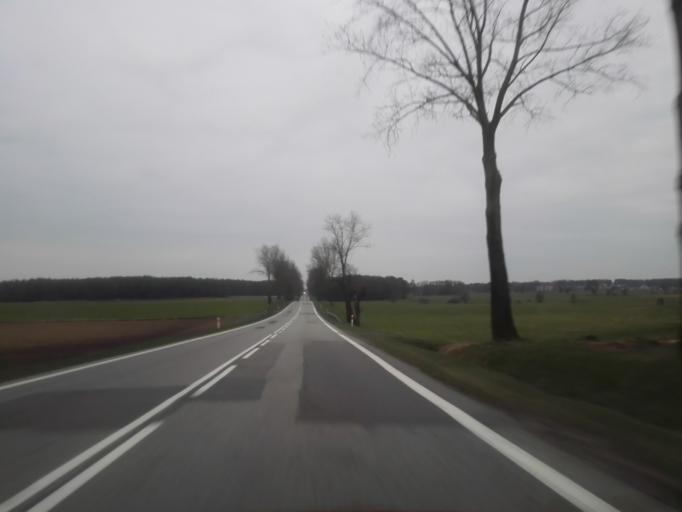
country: PL
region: Podlasie
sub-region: Powiat kolnenski
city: Stawiski
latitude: 53.3179
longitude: 22.1516
